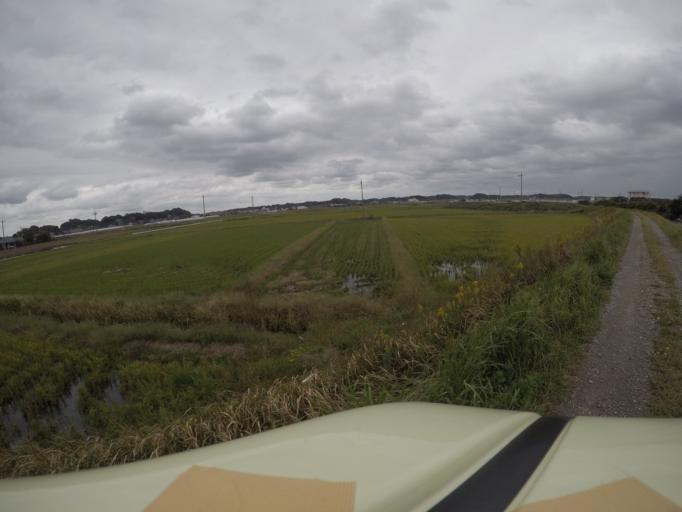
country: JP
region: Ibaraki
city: Ishioka
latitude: 36.1003
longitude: 140.4023
